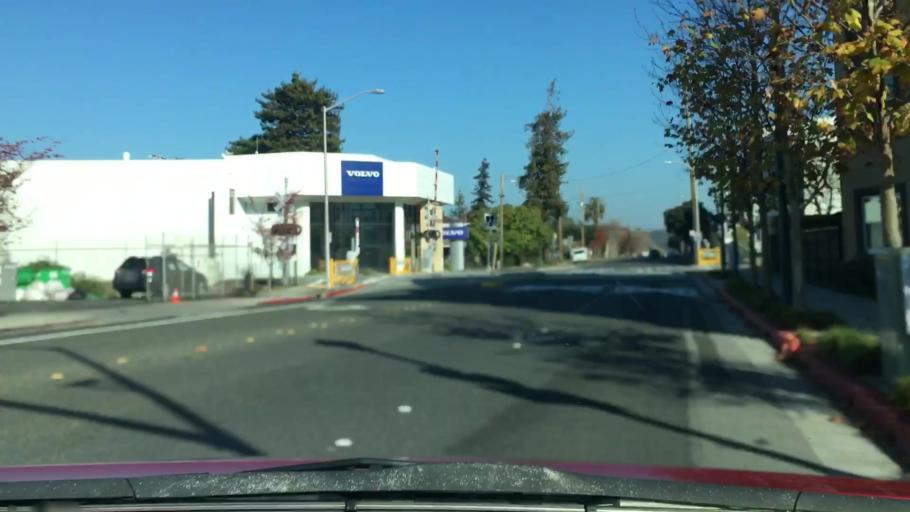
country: US
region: California
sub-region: San Mateo County
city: San Mateo
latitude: 37.5772
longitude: -122.3391
